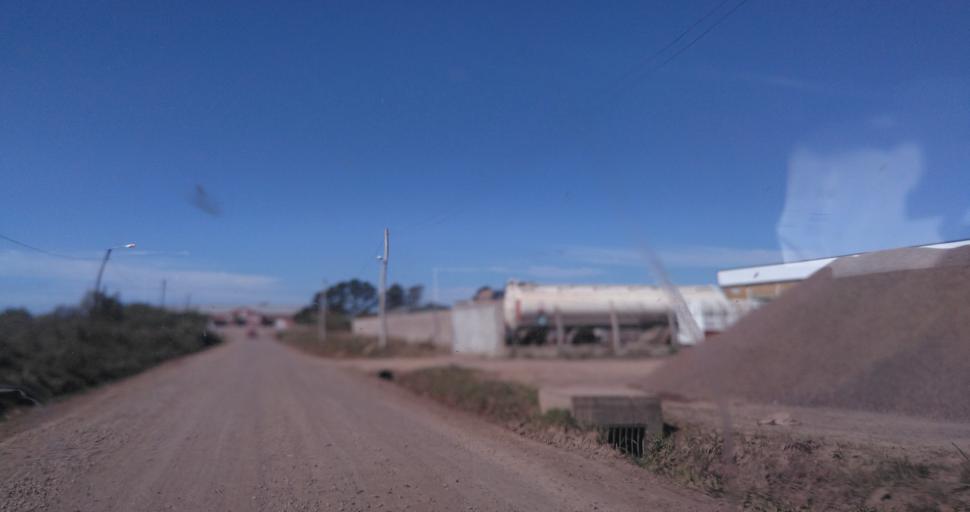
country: AR
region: Chaco
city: Fontana
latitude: -27.4602
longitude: -59.0418
